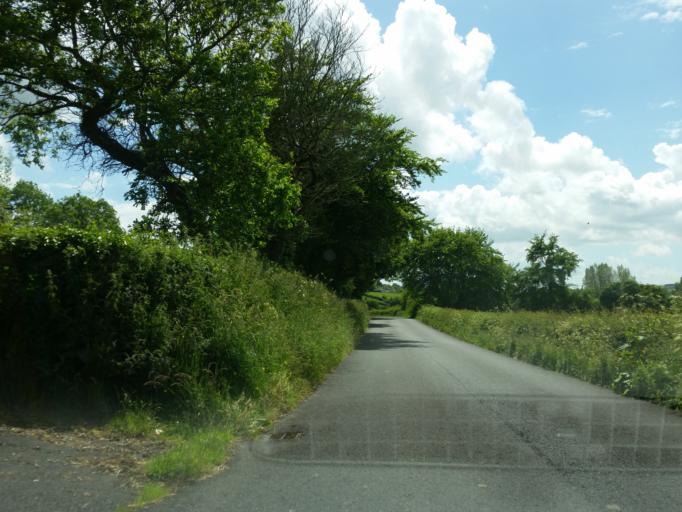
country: GB
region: Northern Ireland
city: Fivemiletown
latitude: 54.3366
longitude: -7.2961
